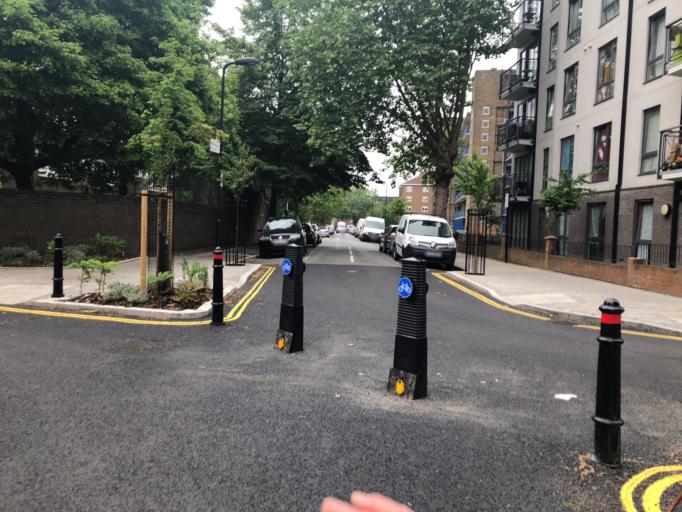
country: GB
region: England
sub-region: Greater London
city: Hackney
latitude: 51.5426
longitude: -0.0520
